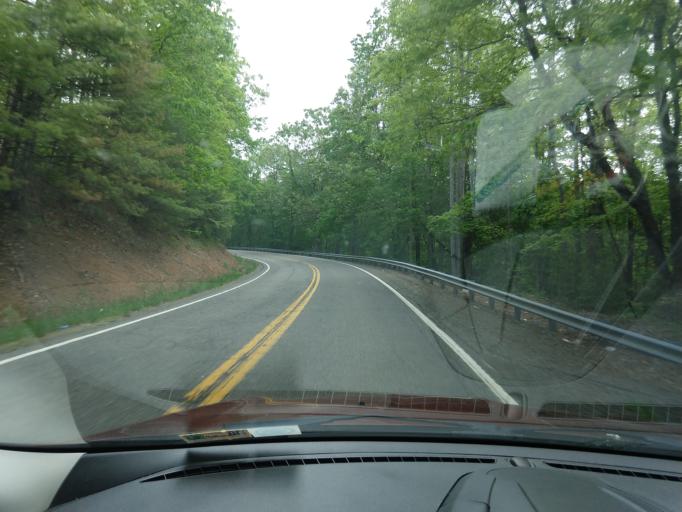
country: US
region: Virginia
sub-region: City of Galax
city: Galax
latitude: 36.7986
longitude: -80.9896
